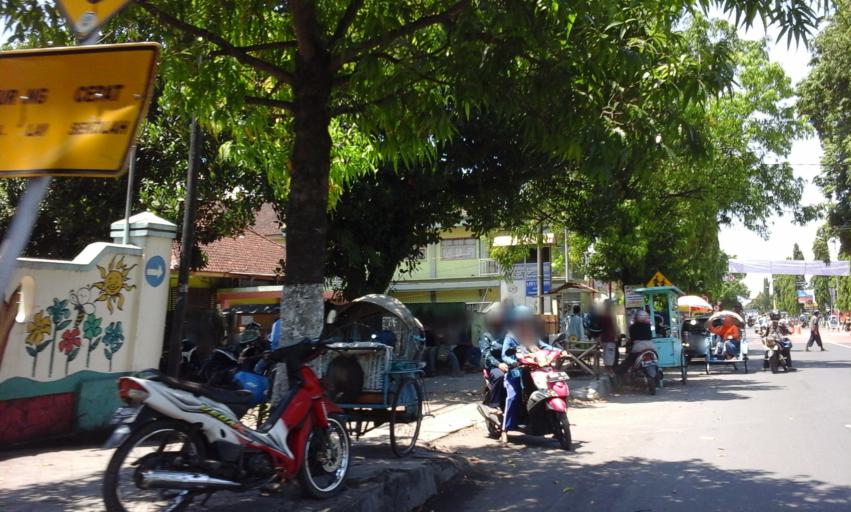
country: ID
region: East Java
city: Krajan
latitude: -8.1622
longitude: 113.7077
